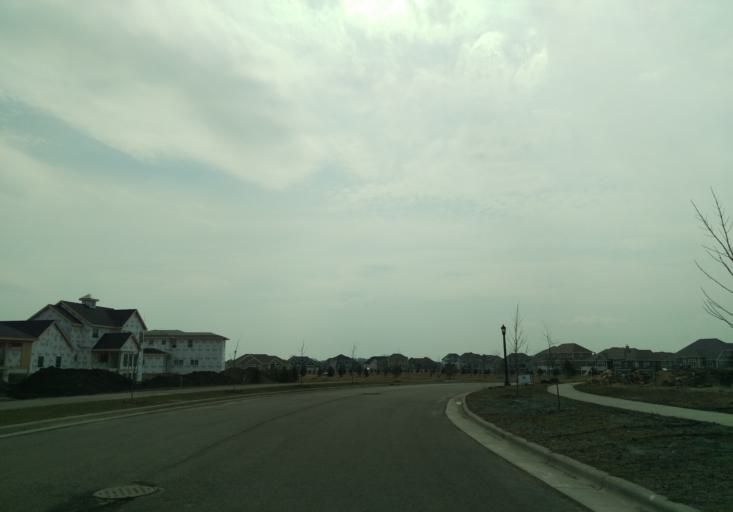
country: US
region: Wisconsin
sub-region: Dane County
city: Waunakee
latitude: 43.1731
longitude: -89.4508
